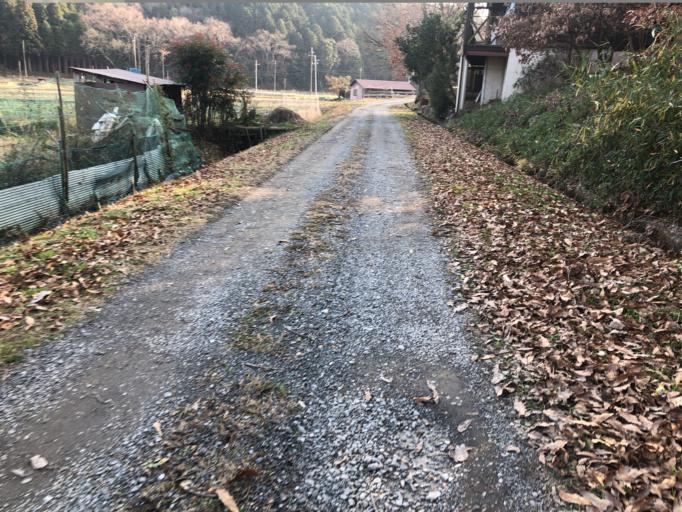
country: JP
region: Kyoto
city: Kameoka
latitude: 35.0569
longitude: 135.4761
